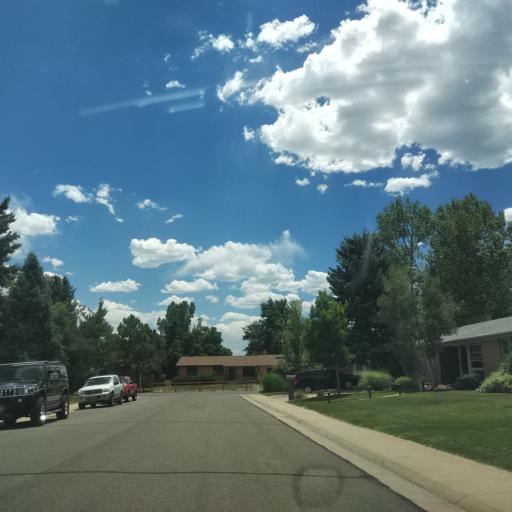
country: US
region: Colorado
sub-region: Jefferson County
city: Lakewood
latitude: 39.6849
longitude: -105.1028
